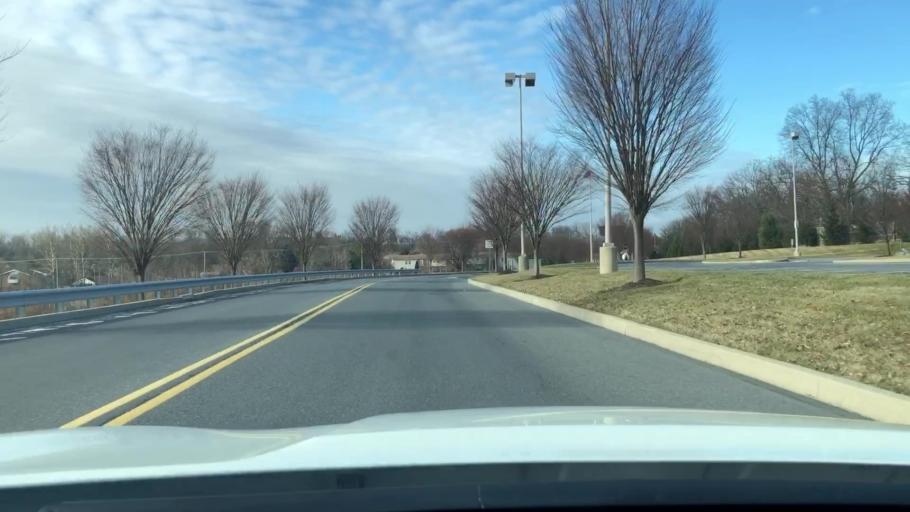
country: US
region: Pennsylvania
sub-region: Lehigh County
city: Fullerton
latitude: 40.6372
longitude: -75.4438
